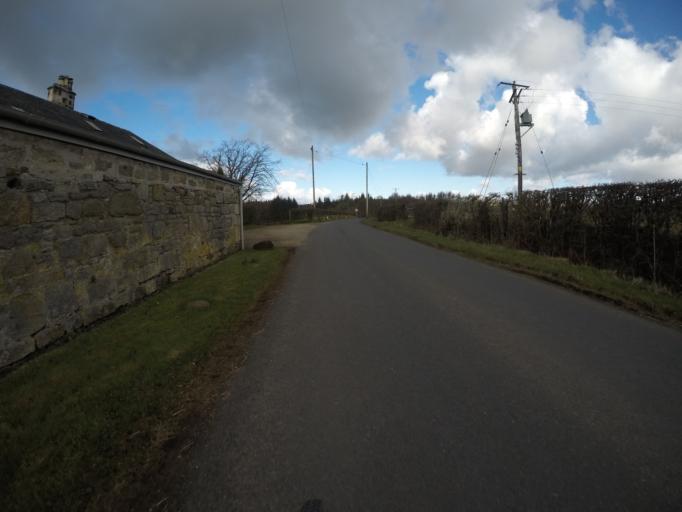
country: GB
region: Scotland
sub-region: North Ayrshire
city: Kilwinning
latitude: 55.6903
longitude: -4.6704
